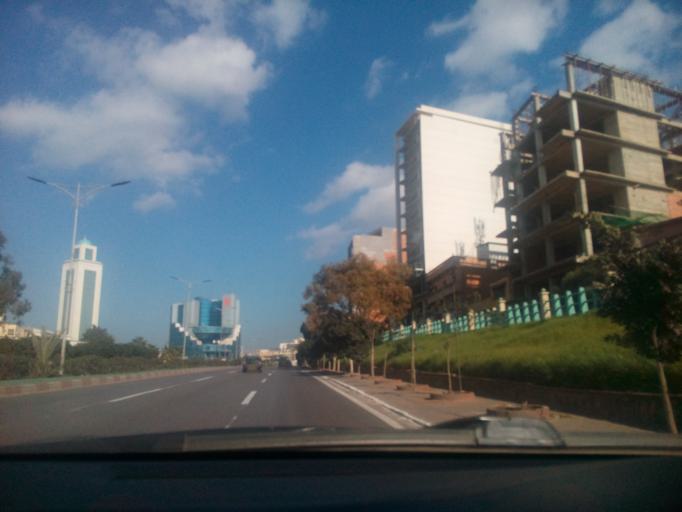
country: DZ
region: Oran
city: Oran
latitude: 35.6939
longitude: -0.6056
